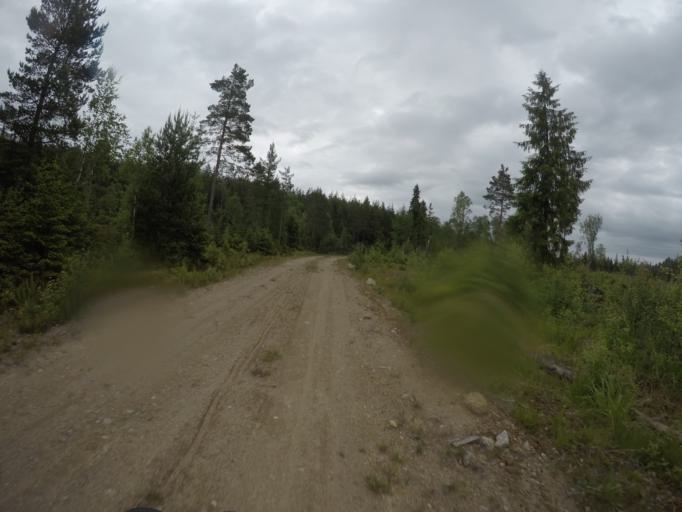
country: SE
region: Dalarna
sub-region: Ludvika Kommun
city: Abborrberget
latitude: 60.0580
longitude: 14.5669
